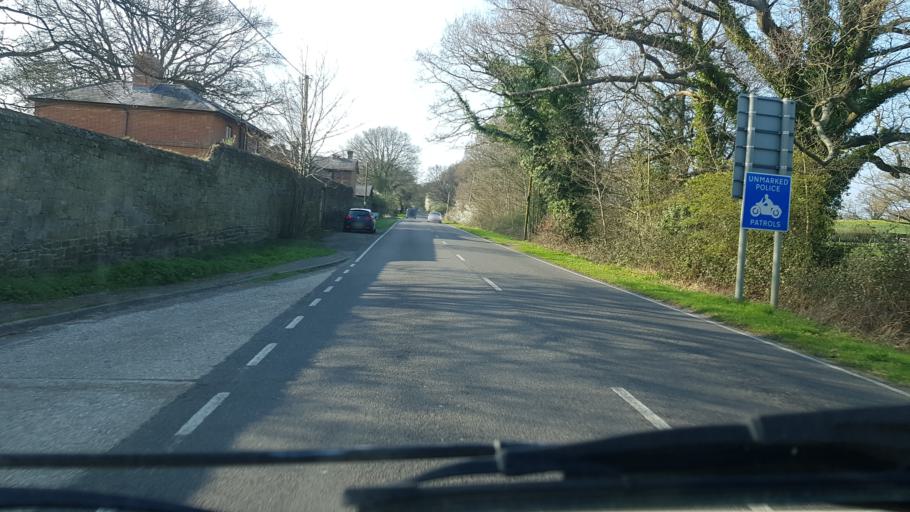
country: GB
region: England
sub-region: West Sussex
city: Petworth
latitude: 50.9965
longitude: -0.6139
